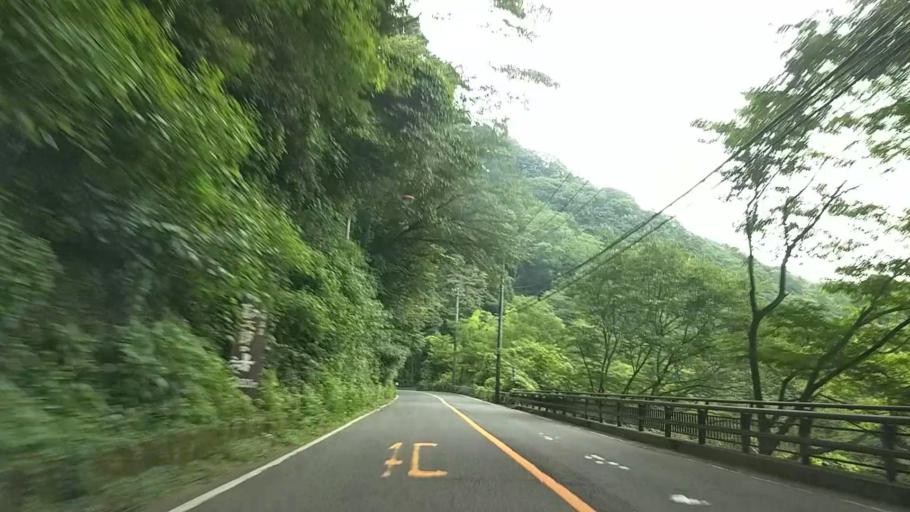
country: JP
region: Kanagawa
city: Hakone
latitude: 35.2460
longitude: 139.0542
